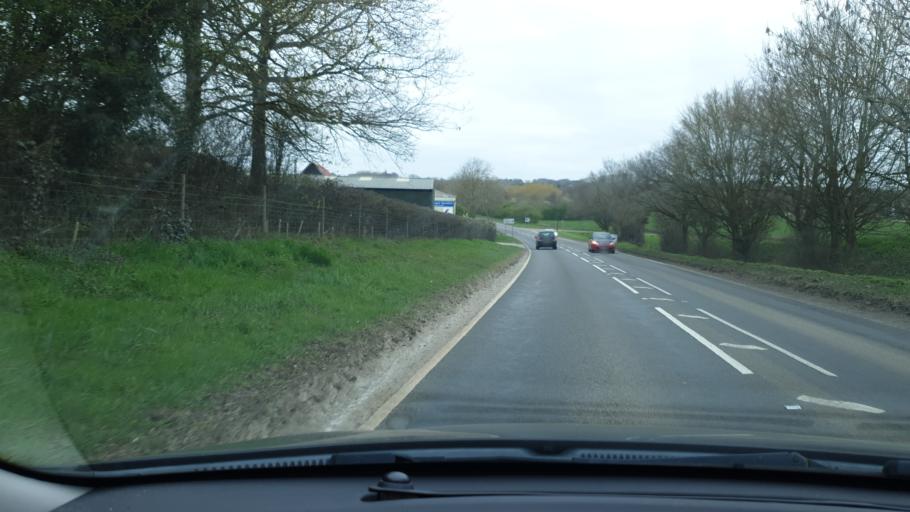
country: GB
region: England
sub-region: Essex
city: Great Horkesley
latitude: 51.9644
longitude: 0.8685
